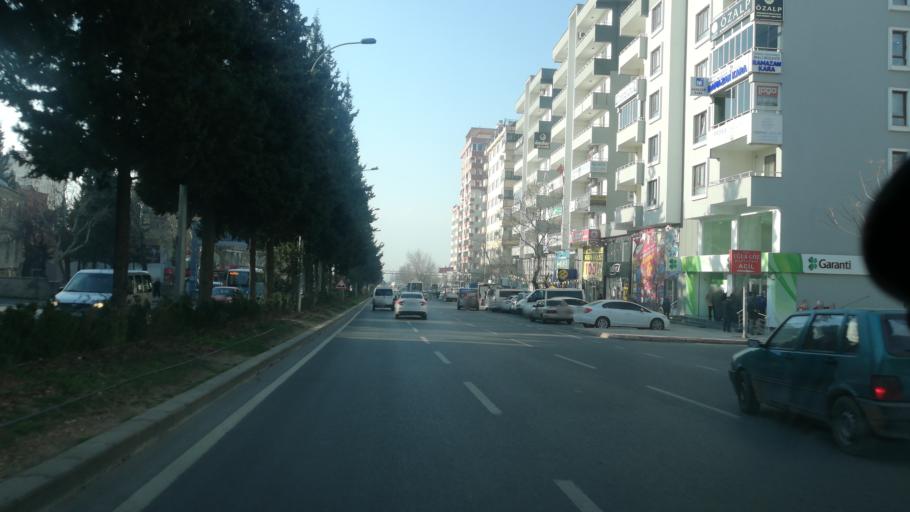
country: TR
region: Kahramanmaras
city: Kahramanmaras
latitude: 37.5722
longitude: 36.9256
